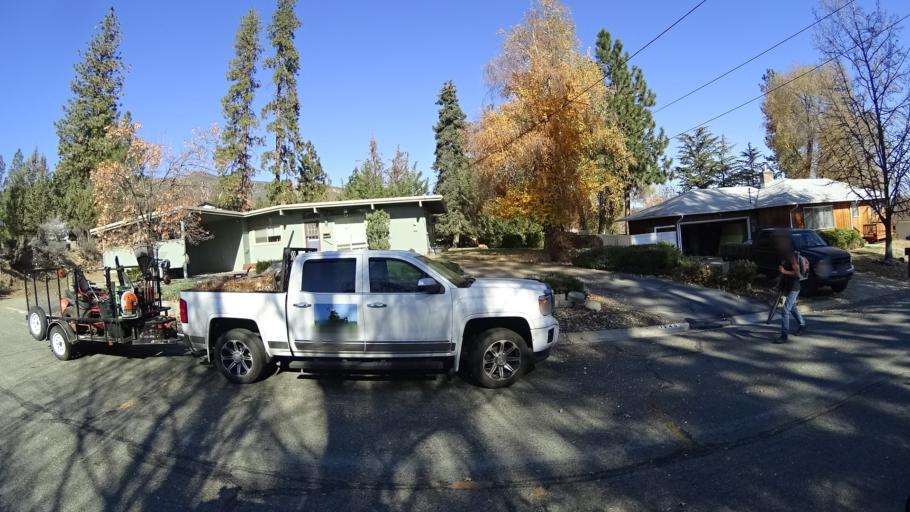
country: US
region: California
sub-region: Siskiyou County
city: Yreka
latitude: 41.7402
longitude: -122.6510
